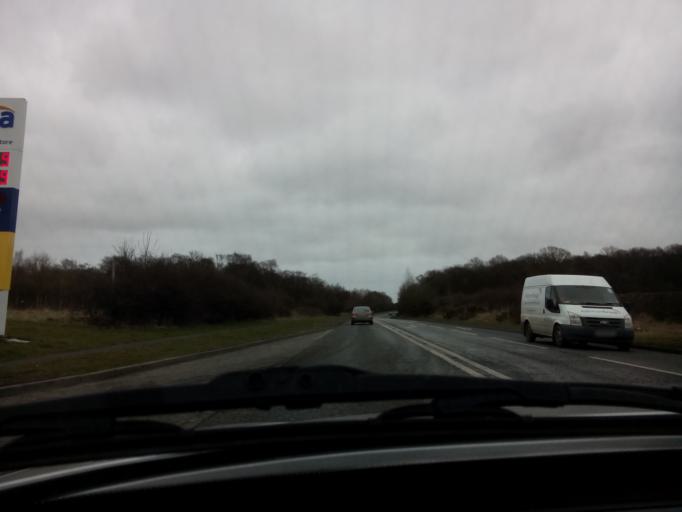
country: GB
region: England
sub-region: County Durham
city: Thornley
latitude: 54.7380
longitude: -1.4145
